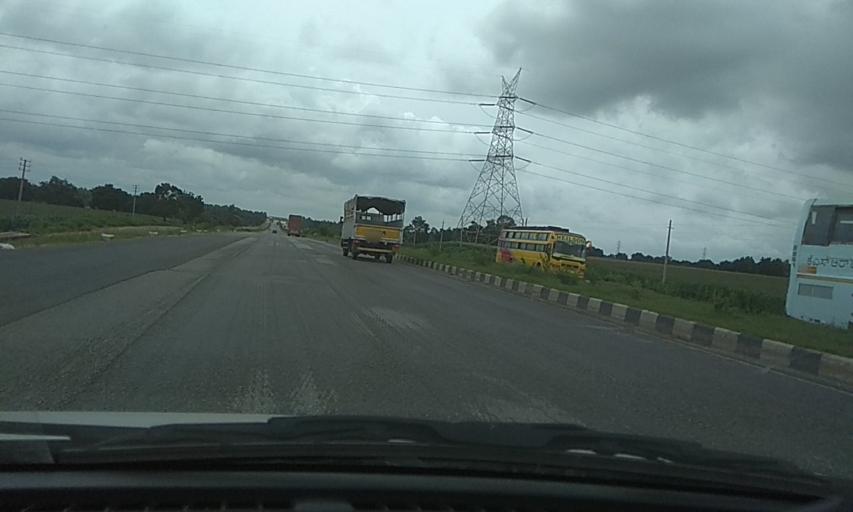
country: IN
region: Karnataka
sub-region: Davanagere
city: Mayakonda
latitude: 14.3695
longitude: 76.1356
